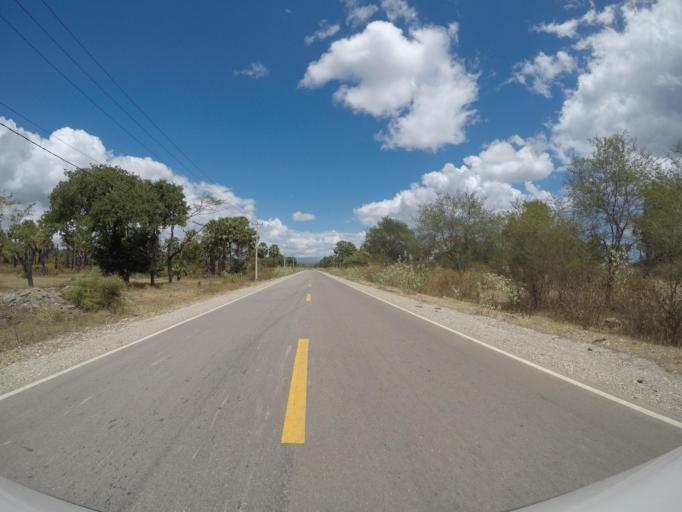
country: TL
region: Lautem
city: Lospalos
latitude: -8.3826
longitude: 126.8604
